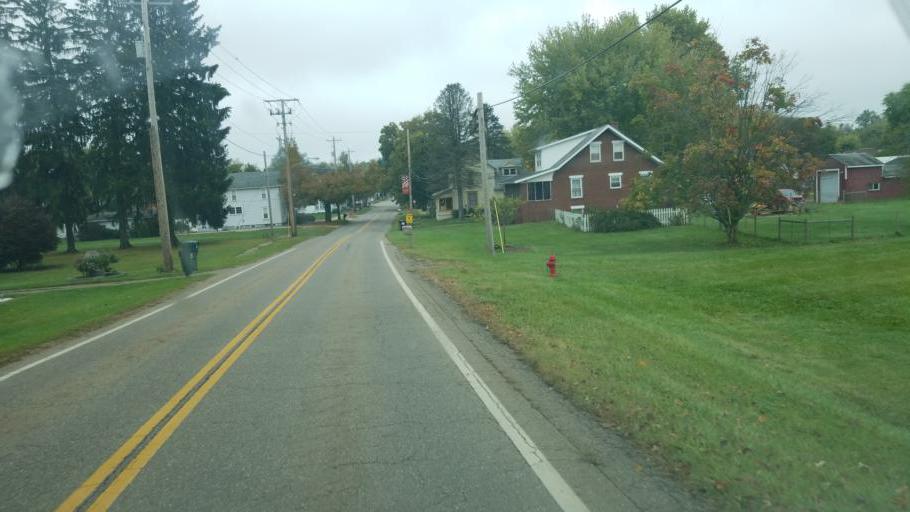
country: US
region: Ohio
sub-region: Carroll County
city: Lake Mohawk
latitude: 40.6490
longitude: -81.2987
